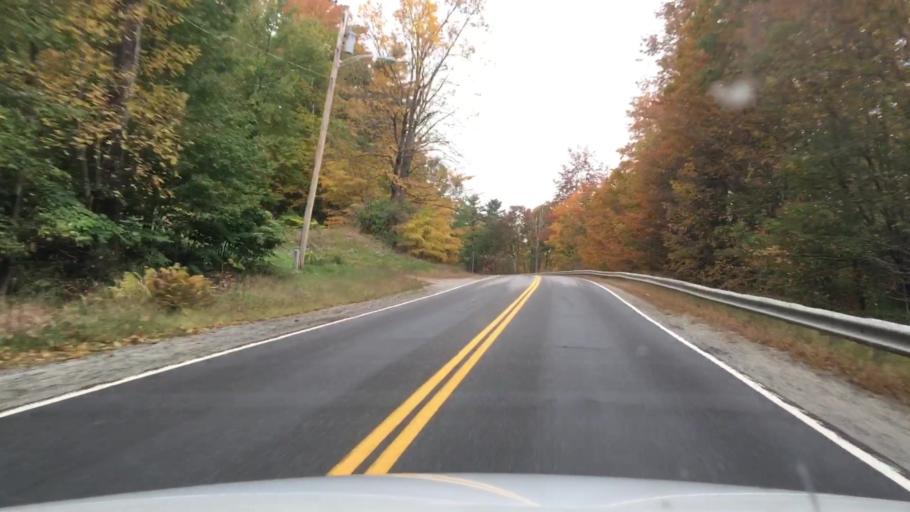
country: US
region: Maine
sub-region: Oxford County
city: Bethel
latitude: 44.4056
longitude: -70.7981
